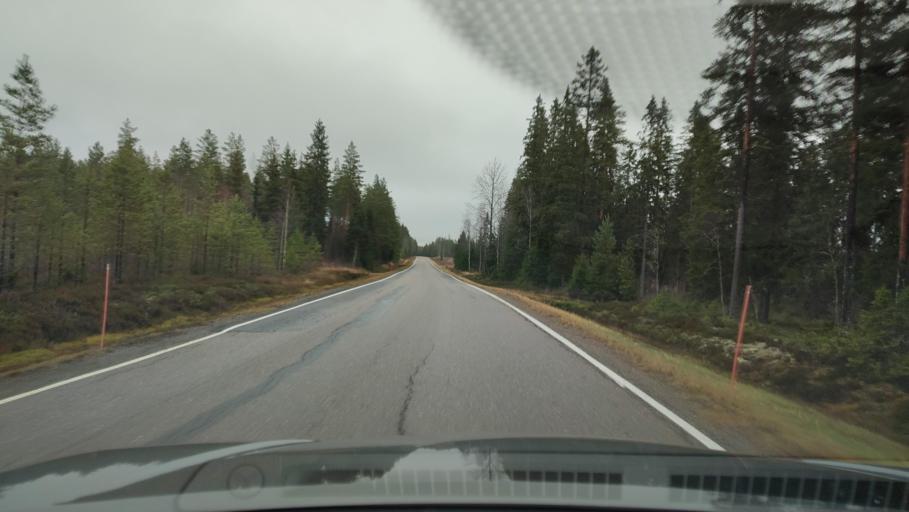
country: FI
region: Southern Ostrobothnia
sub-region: Suupohja
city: Isojoki
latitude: 62.2138
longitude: 21.9854
